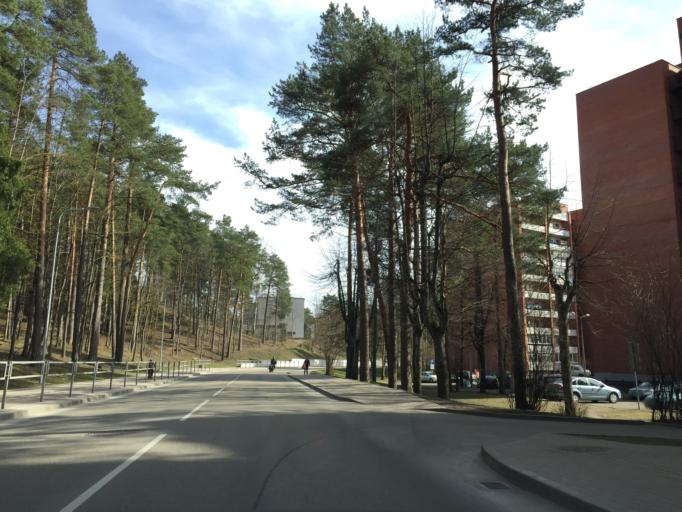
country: LV
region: Ogre
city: Ogre
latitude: 56.8214
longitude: 24.6047
